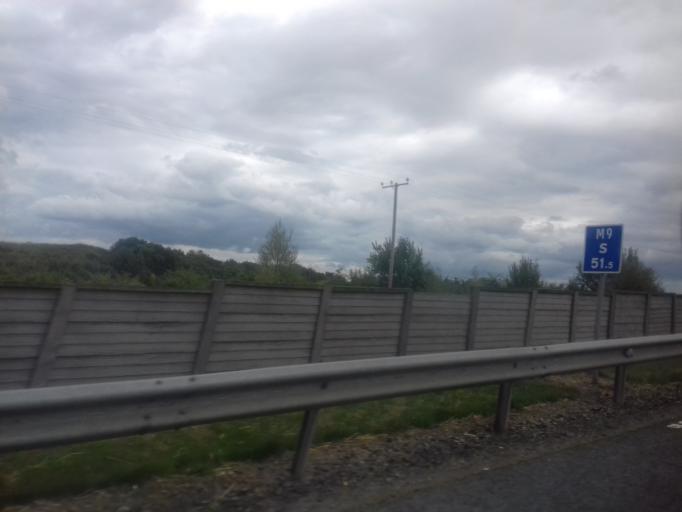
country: IE
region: Leinster
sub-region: County Carlow
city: Bagenalstown
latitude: 52.7700
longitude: -6.9517
